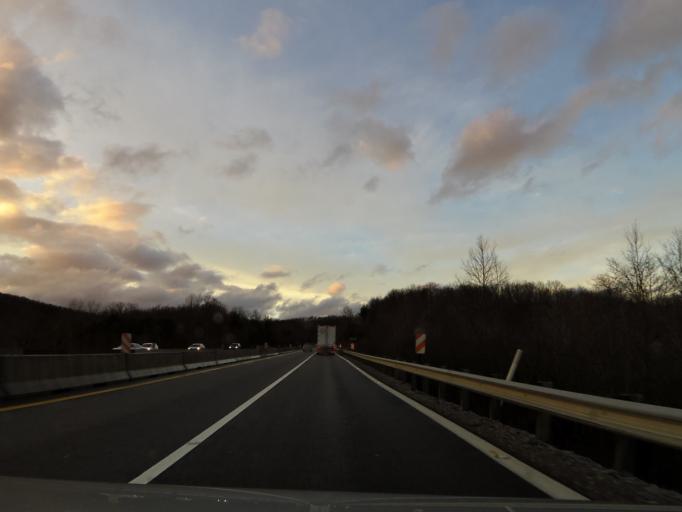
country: US
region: Tennessee
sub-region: Campbell County
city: Jacksboro
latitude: 36.4249
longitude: -84.2893
